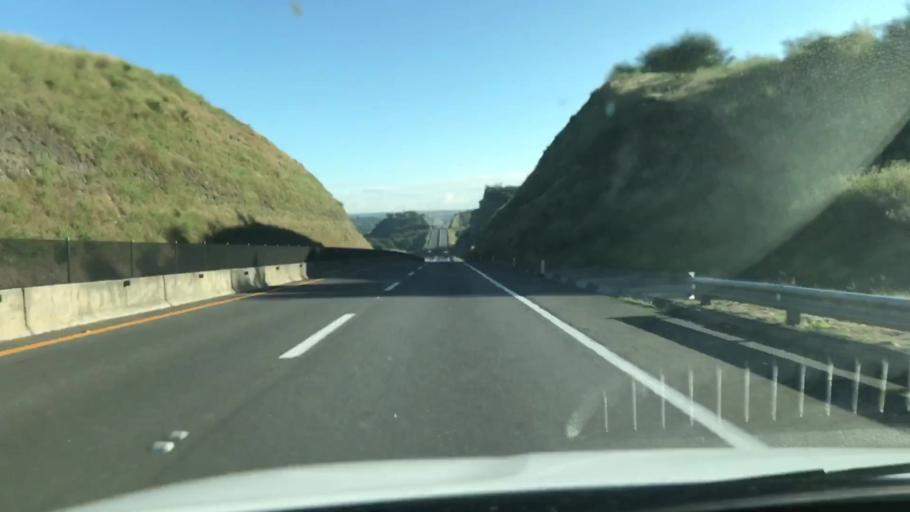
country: MX
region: Jalisco
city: Jalostotitlan
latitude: 21.1442
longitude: -102.4313
